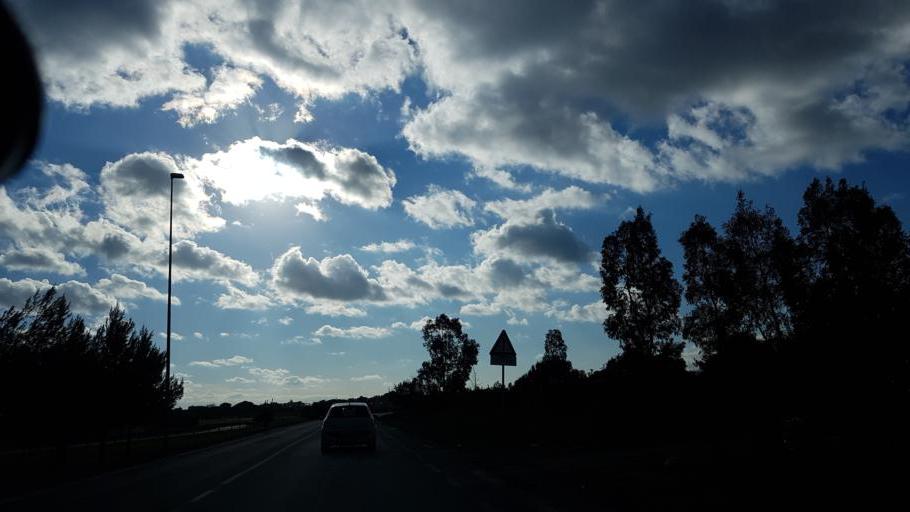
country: IT
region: Apulia
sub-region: Provincia di Brindisi
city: Brindisi
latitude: 40.6530
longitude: 17.9323
